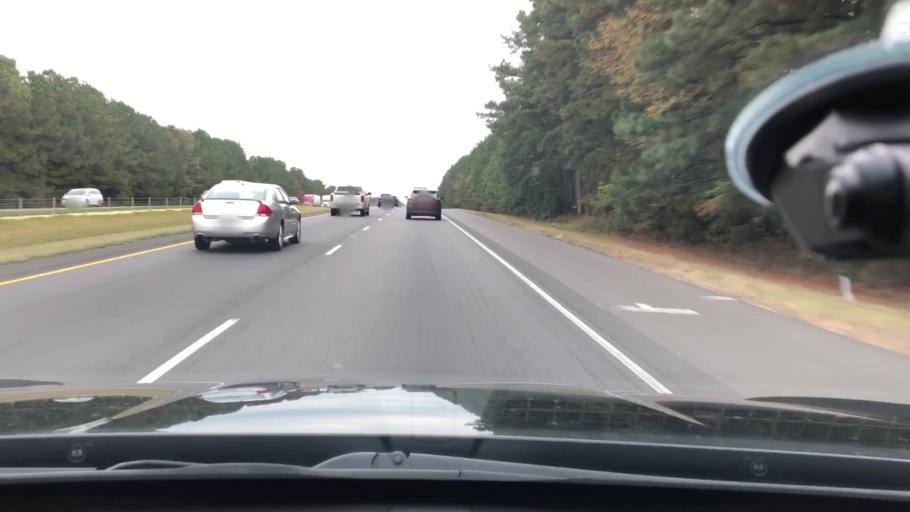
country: US
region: Arkansas
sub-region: Clark County
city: Arkadelphia
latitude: 34.0442
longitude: -93.1381
